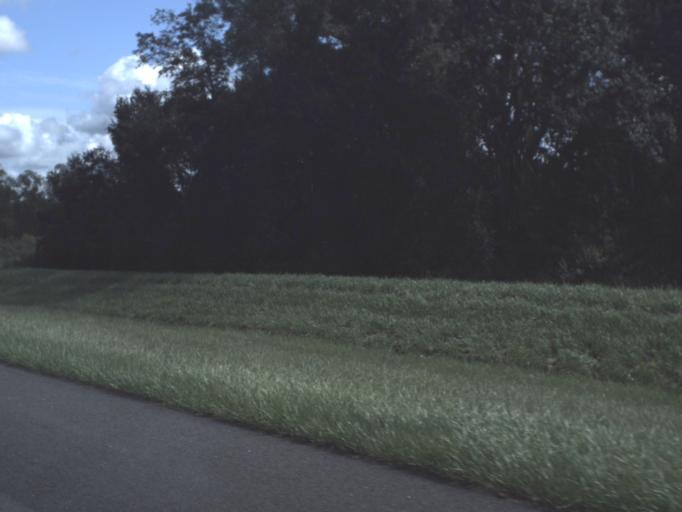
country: US
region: Florida
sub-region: Hillsborough County
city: Plant City
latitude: 28.0558
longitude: -82.1357
